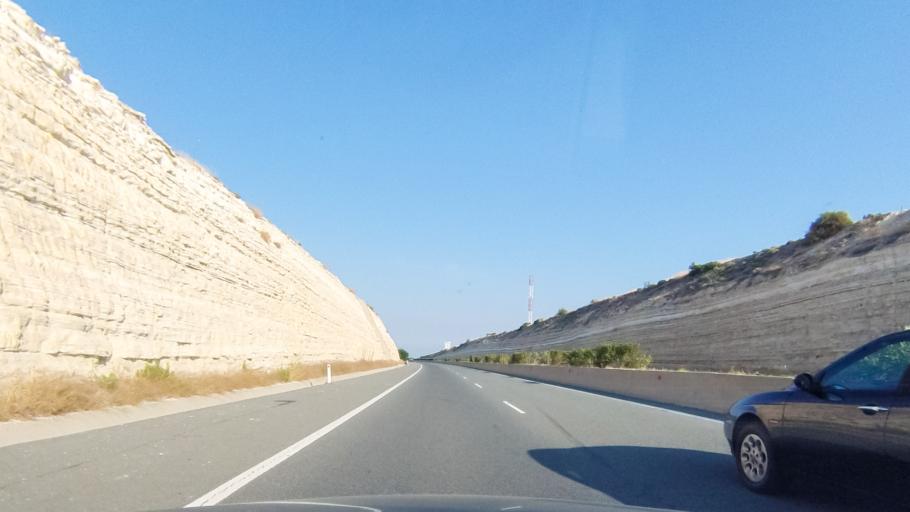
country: CY
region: Limassol
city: Sotira
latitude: 34.6868
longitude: 32.8752
